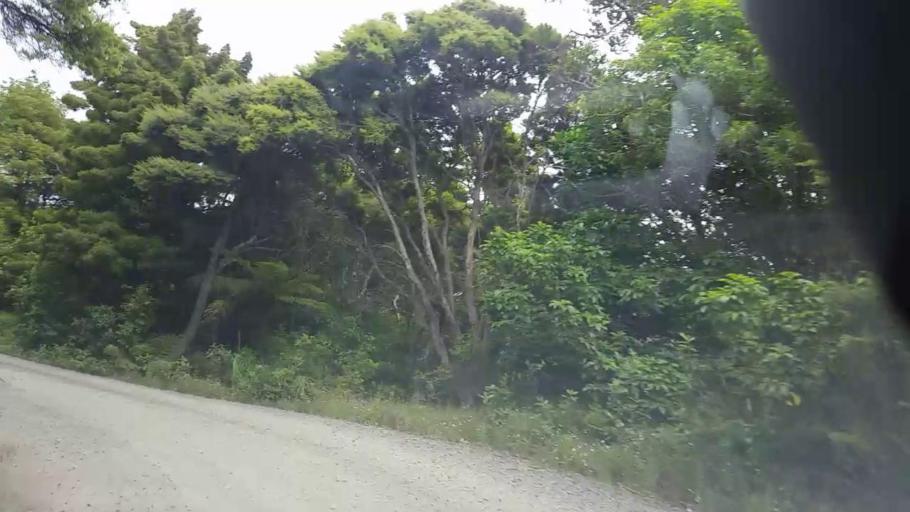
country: NZ
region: Auckland
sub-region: Auckland
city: Titirangi
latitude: -37.0305
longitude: 174.5243
